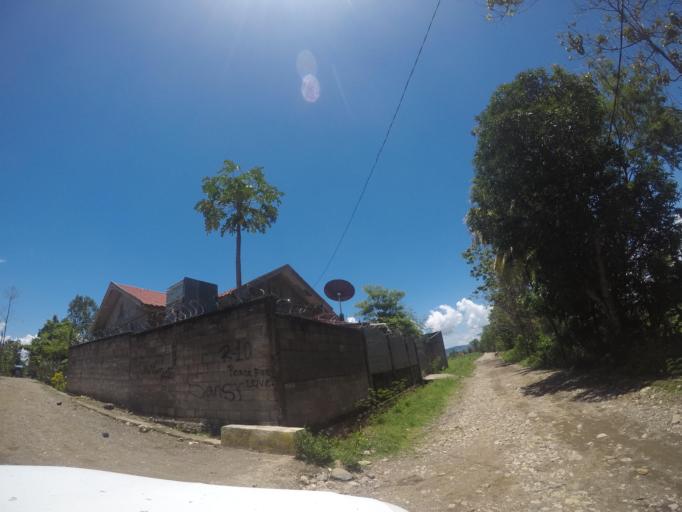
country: TL
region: Bobonaro
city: Maliana
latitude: -8.9864
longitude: 125.2149
